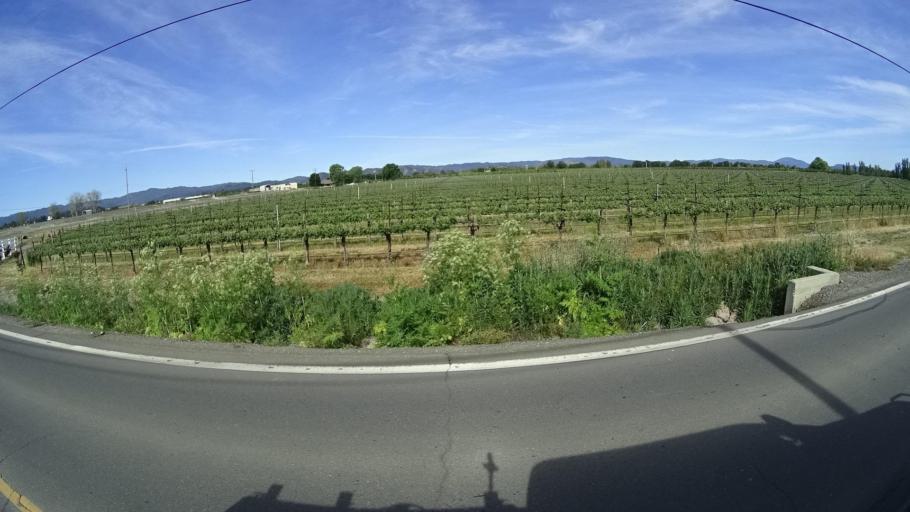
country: US
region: California
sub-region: Lake County
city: Kelseyville
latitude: 38.9933
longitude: -122.8290
